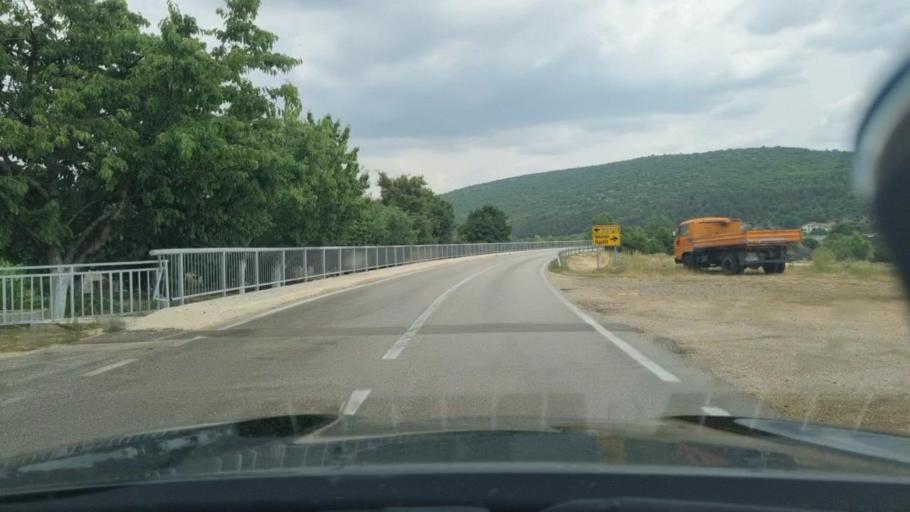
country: BA
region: Federation of Bosnia and Herzegovina
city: Podhum
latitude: 43.6877
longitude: 17.0811
